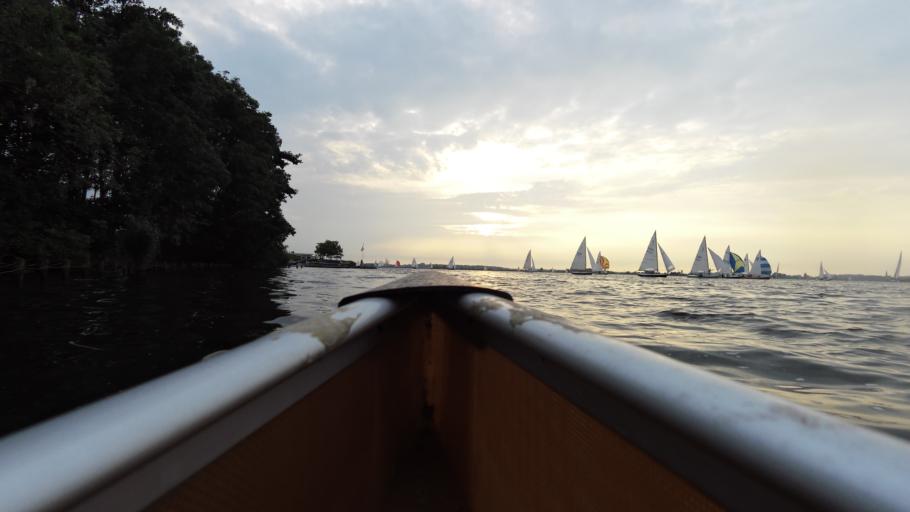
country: NL
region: South Holland
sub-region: Gemeente Teylingen
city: Sassenheim
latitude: 52.2015
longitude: 4.5517
